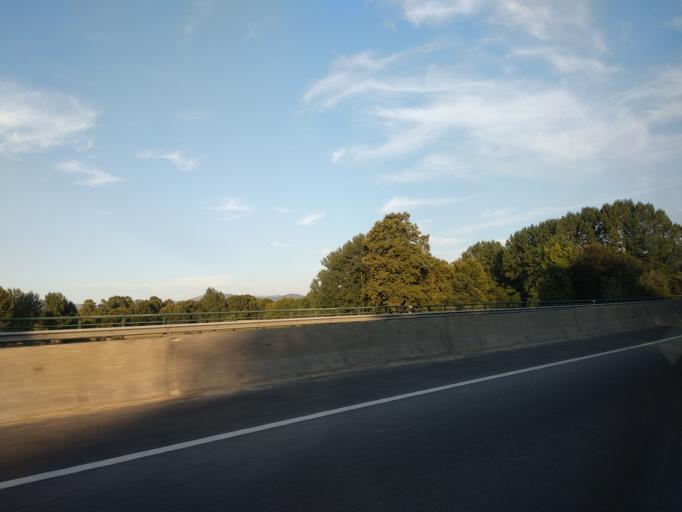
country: PT
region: Braga
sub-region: Vila Verde
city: Prado
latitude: 41.6041
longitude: -8.4509
